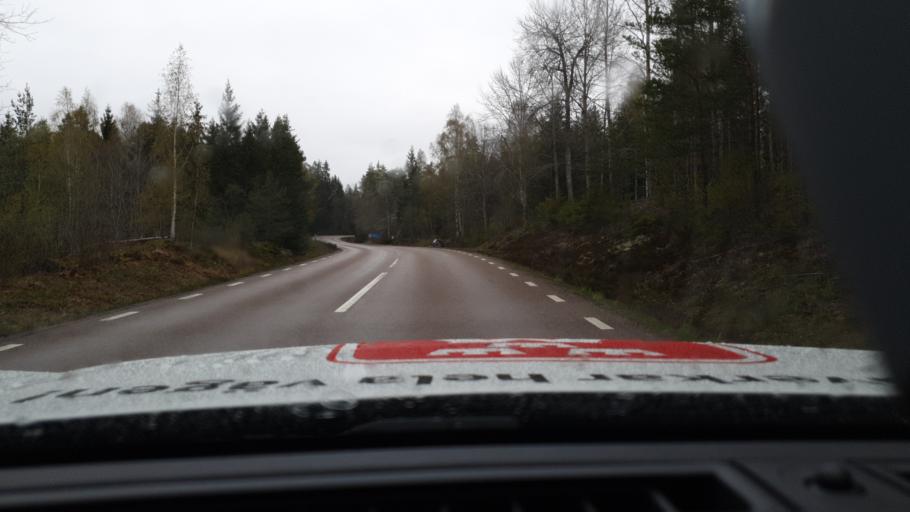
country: SE
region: Soedermanland
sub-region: Strangnas Kommun
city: Mariefred
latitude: 59.1921
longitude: 17.1847
